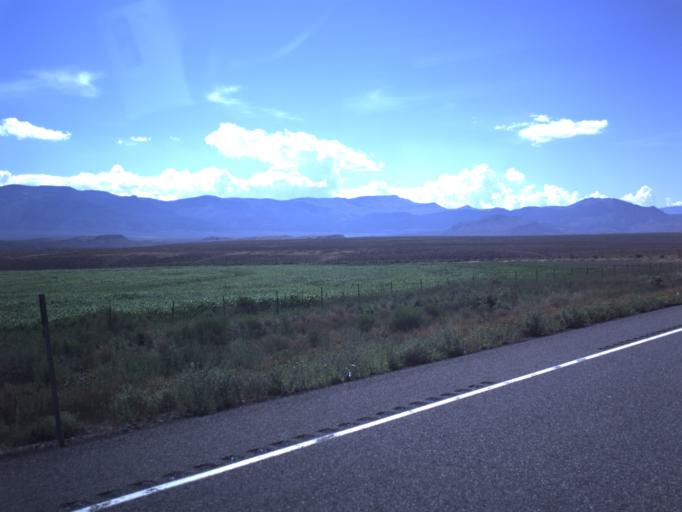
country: US
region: Utah
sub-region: Piute County
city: Junction
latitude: 38.4183
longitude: -112.2315
